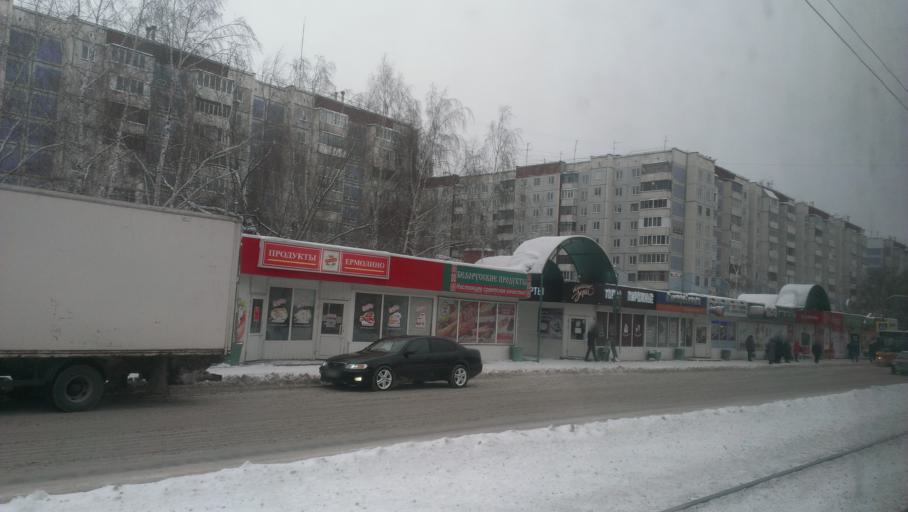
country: RU
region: Altai Krai
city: Novosilikatnyy
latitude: 53.3412
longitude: 83.6704
